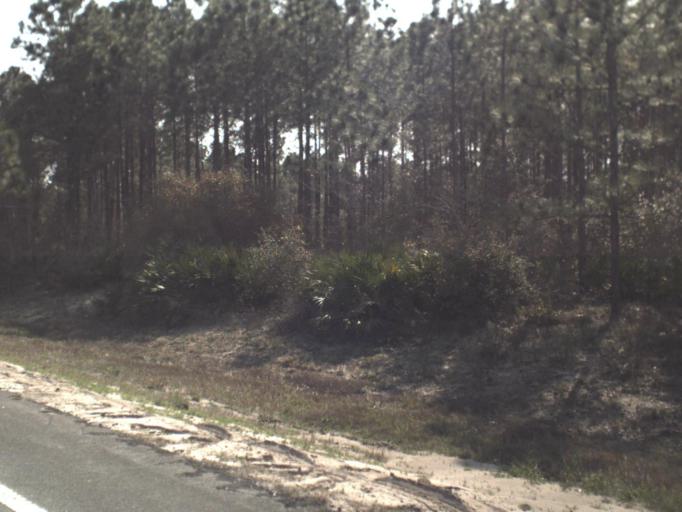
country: US
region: Florida
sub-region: Franklin County
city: Carrabelle
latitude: 29.9206
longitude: -84.5203
